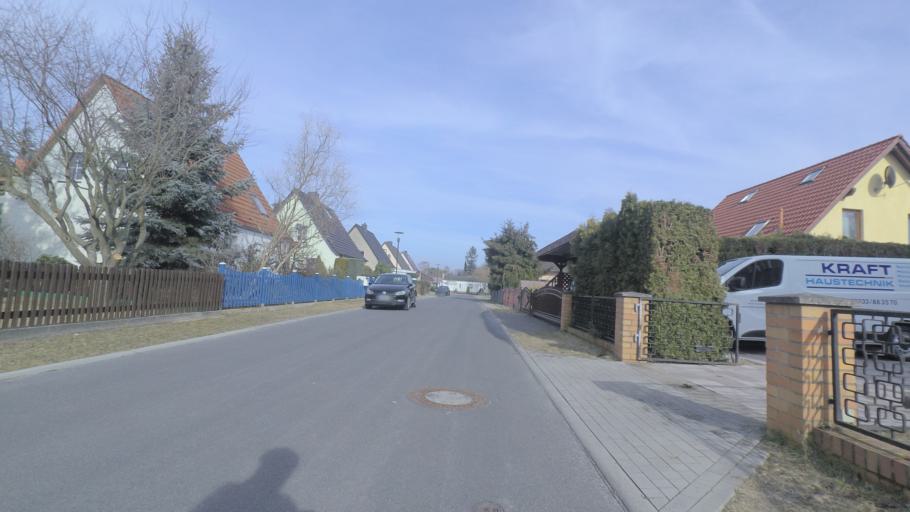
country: DE
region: Brandenburg
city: Ludwigsfelde
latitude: 52.2916
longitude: 13.2603
